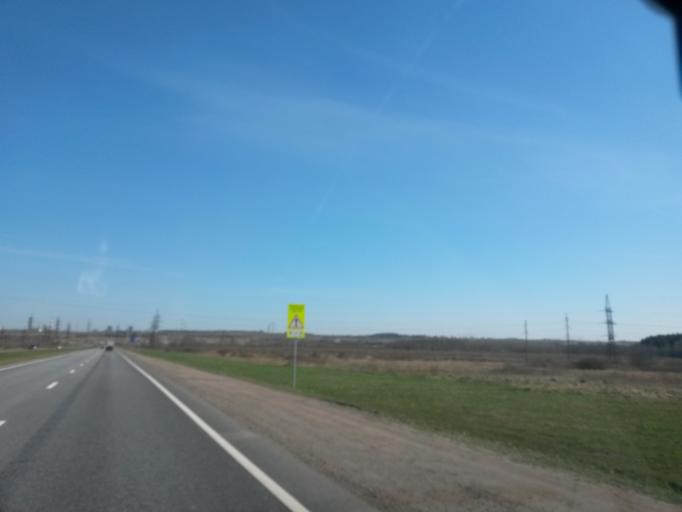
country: RU
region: Jaroslavl
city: Krasnyye Tkachi
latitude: 57.5065
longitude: 39.7868
